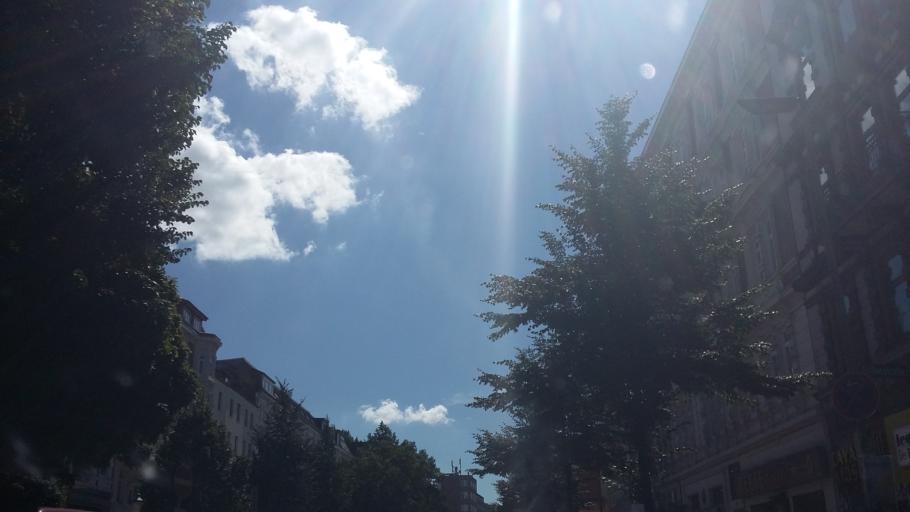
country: DE
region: Hamburg
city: St. Pauli
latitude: 53.5630
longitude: 9.9609
